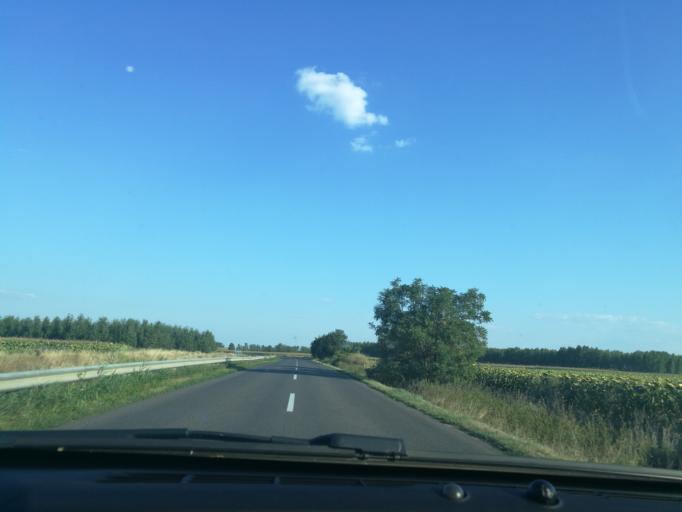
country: HU
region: Szabolcs-Szatmar-Bereg
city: Tiszabercel
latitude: 48.1404
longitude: 21.6421
